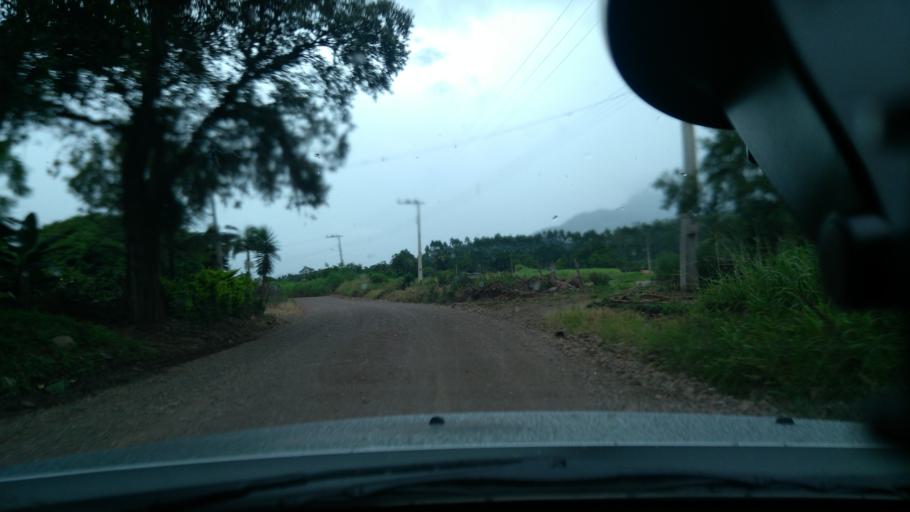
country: BR
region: Rio Grande do Sul
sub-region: Torres
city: Torres
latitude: -29.2106
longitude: -49.9804
